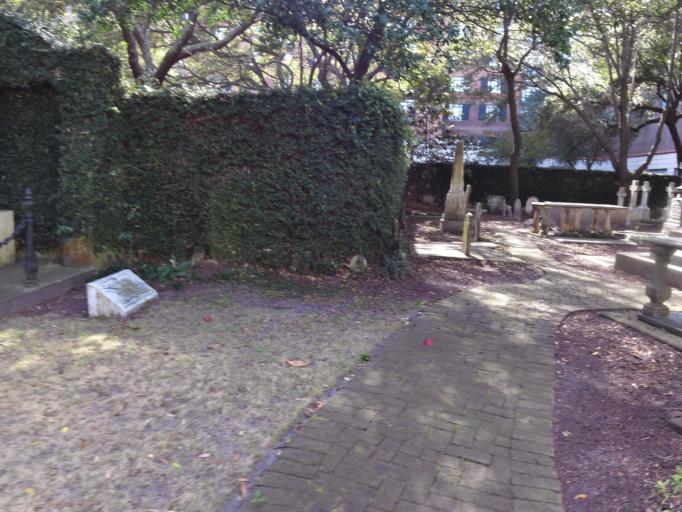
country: US
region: South Carolina
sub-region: Charleston County
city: Charleston
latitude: 32.7817
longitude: -79.9326
